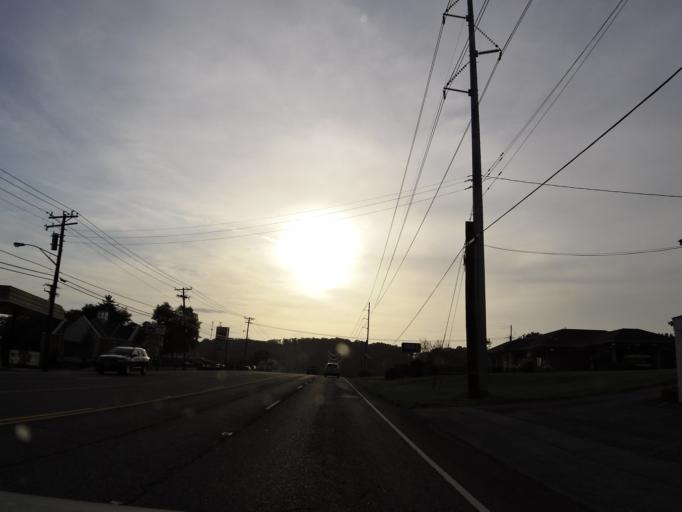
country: US
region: Tennessee
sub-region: Sevier County
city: Seymour
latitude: 35.8832
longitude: -83.7888
